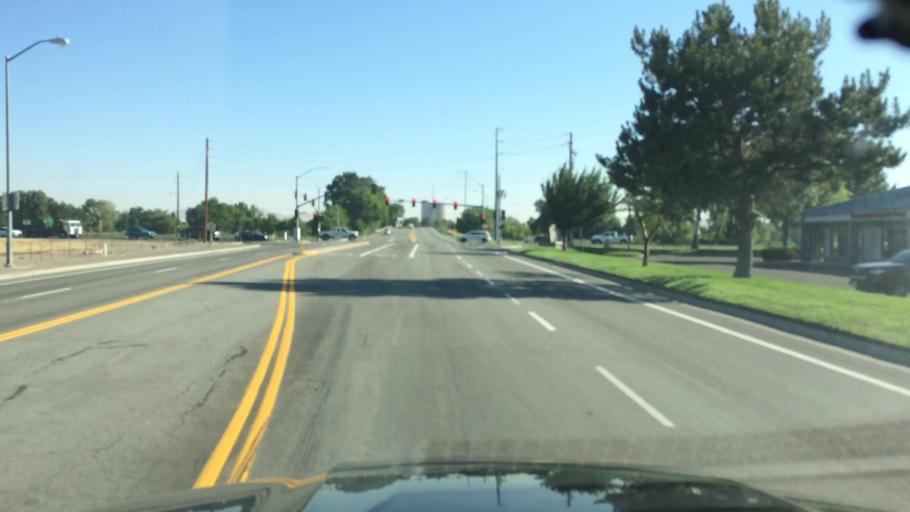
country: US
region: Nevada
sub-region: Washoe County
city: Sparks
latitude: 39.5148
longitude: -119.7620
